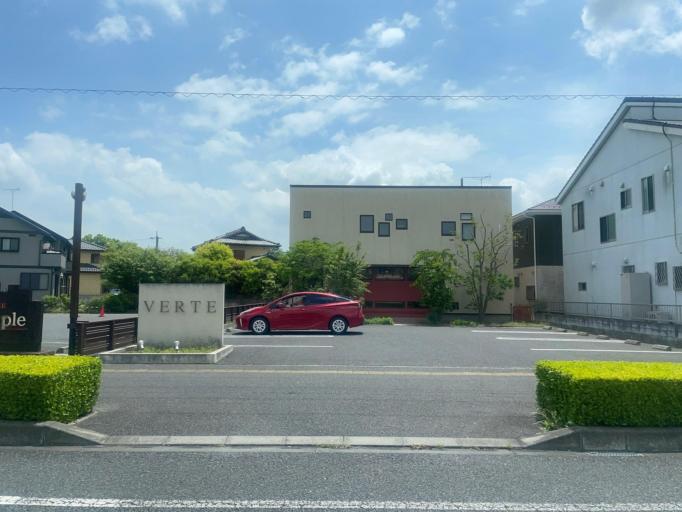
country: JP
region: Tochigi
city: Tochigi
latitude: 36.3903
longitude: 139.7288
